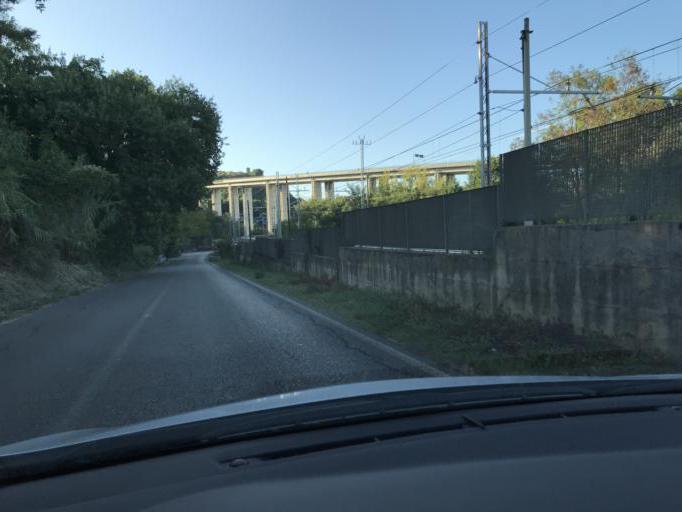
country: IT
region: Latium
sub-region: Provincia di Viterbo
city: Orte
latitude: 42.4488
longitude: 12.3908
